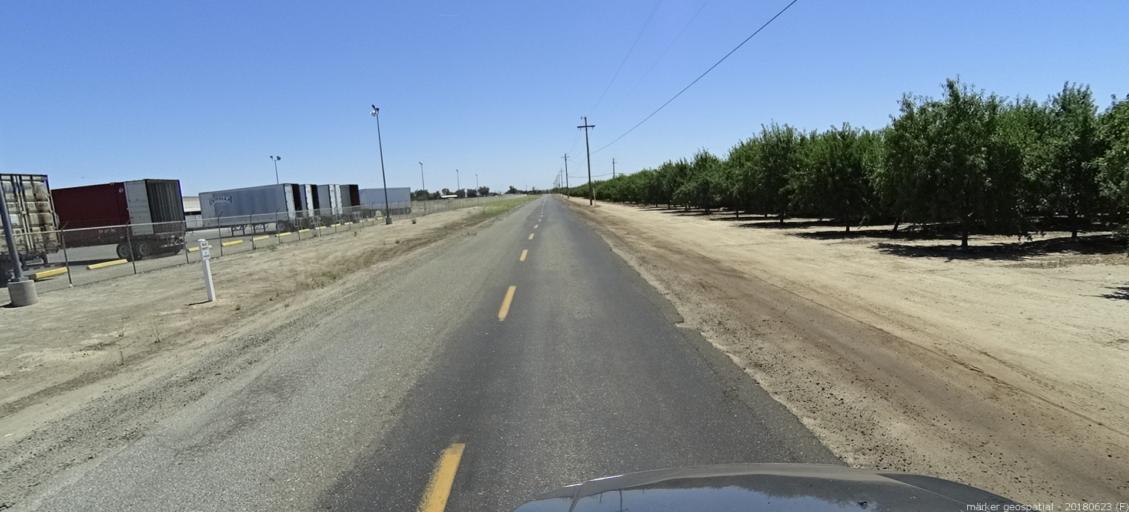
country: US
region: California
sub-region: Madera County
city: Fairmead
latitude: 37.0911
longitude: -120.2225
